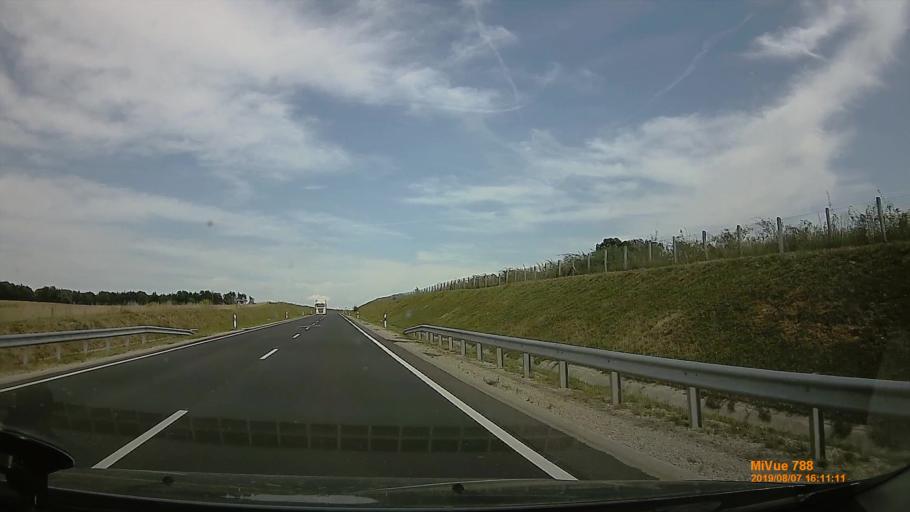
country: HU
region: Zala
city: Zalalovo
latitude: 46.8718
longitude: 16.6166
